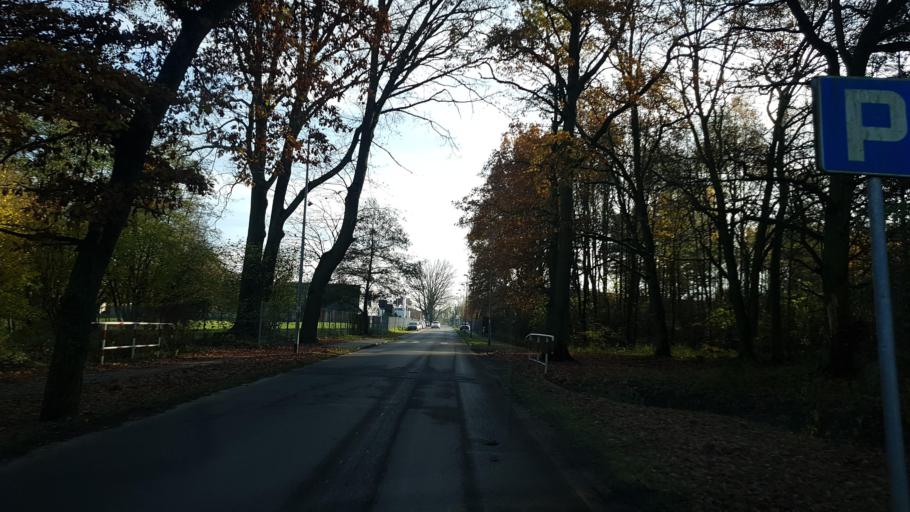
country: PL
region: West Pomeranian Voivodeship
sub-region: Powiat policki
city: Dobra
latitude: 53.4899
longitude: 14.3774
